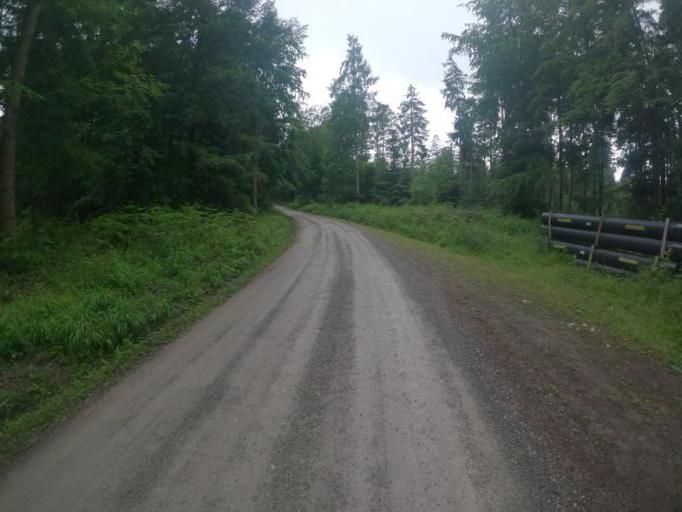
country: DE
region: Baden-Wuerttemberg
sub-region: Regierungsbezirk Stuttgart
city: Schorndorf
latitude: 48.7685
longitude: 9.5384
